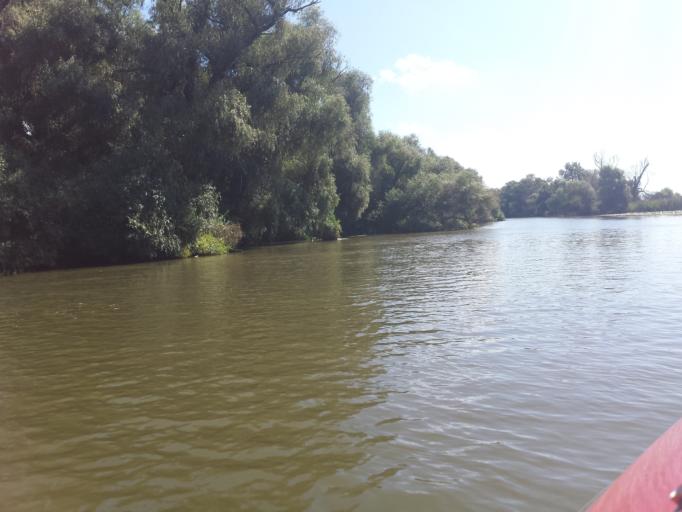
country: RO
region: Tulcea
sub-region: Comuna Mahmudia
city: Mahmudia
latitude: 45.2154
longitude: 29.1799
